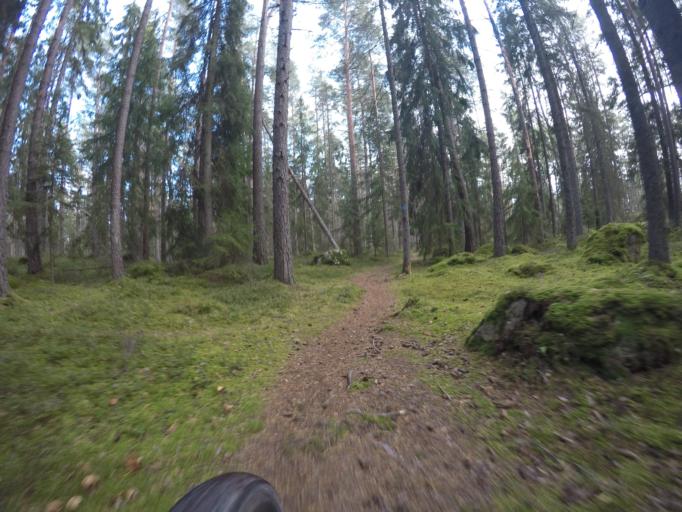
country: SE
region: Vaestmanland
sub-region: Kopings Kommun
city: Koping
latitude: 59.5332
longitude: 15.9989
